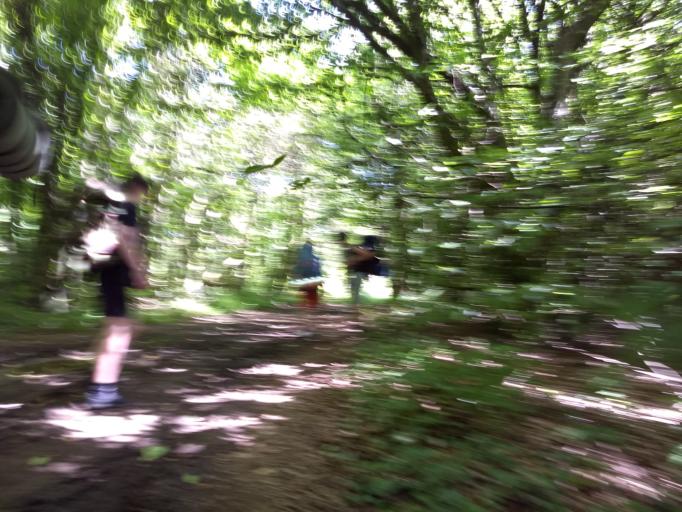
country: GB
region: England
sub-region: Isle of Wight
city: Shalfleet
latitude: 50.6610
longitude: -1.3859
